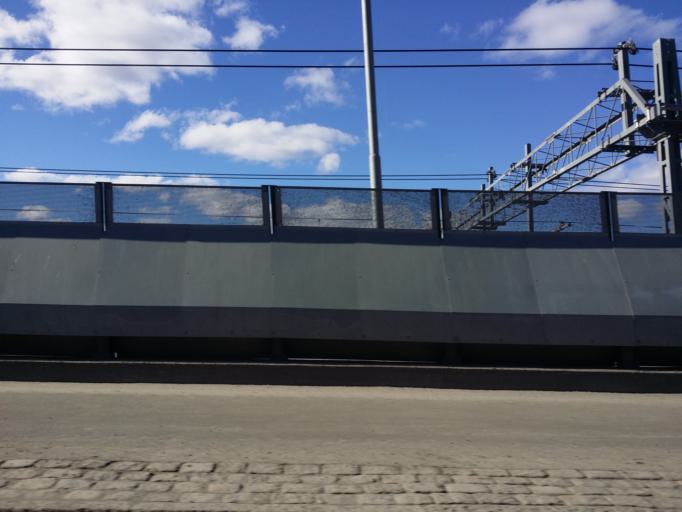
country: NO
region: Oslo
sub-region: Oslo
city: Oslo
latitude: 59.9000
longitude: 10.7575
